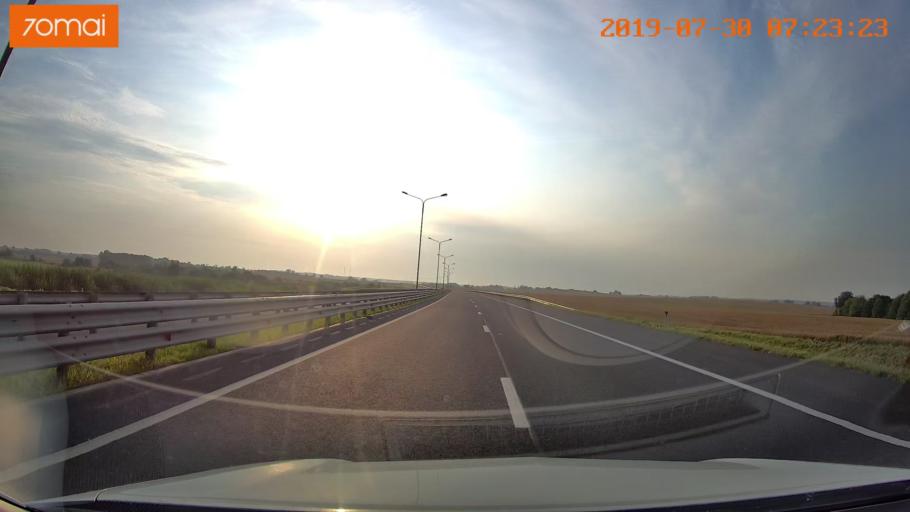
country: RU
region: Kaliningrad
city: Bol'shoe Isakovo
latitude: 54.6918
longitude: 20.7824
